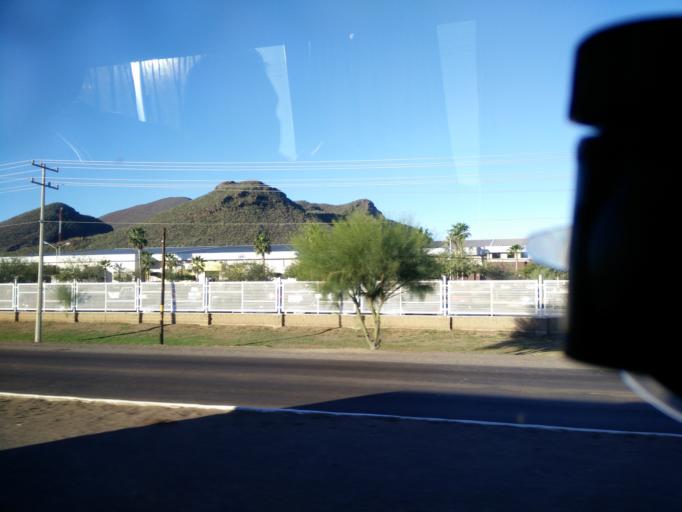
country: MX
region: Sonora
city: Heroica Guaymas
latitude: 27.9577
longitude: -110.9352
